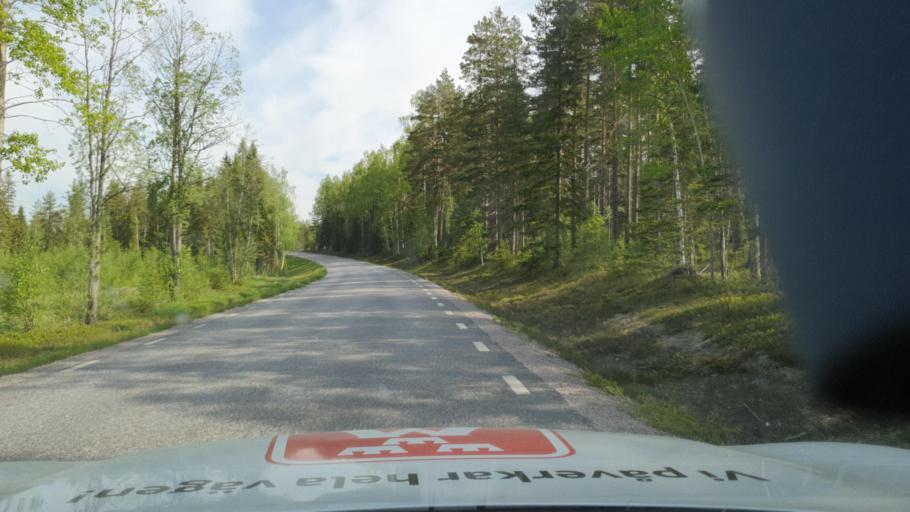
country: SE
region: Vaesterbotten
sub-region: Vannas Kommun
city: Vannasby
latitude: 63.8080
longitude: 19.8546
